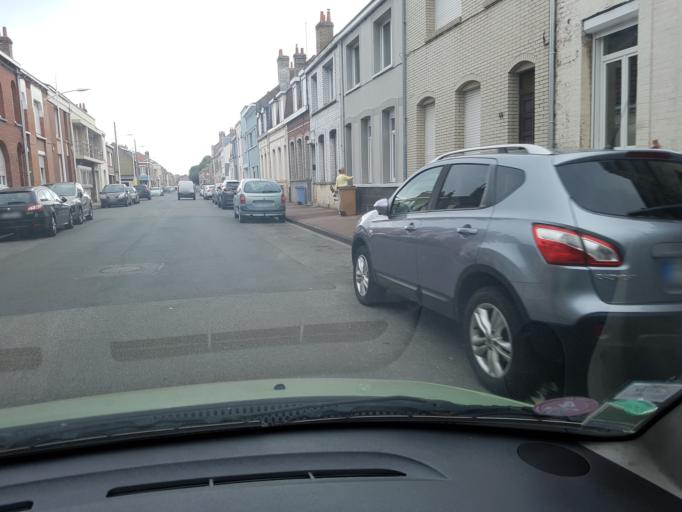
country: FR
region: Nord-Pas-de-Calais
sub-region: Departement du Nord
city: Coudekerque-Branche
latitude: 51.0211
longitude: 2.3832
